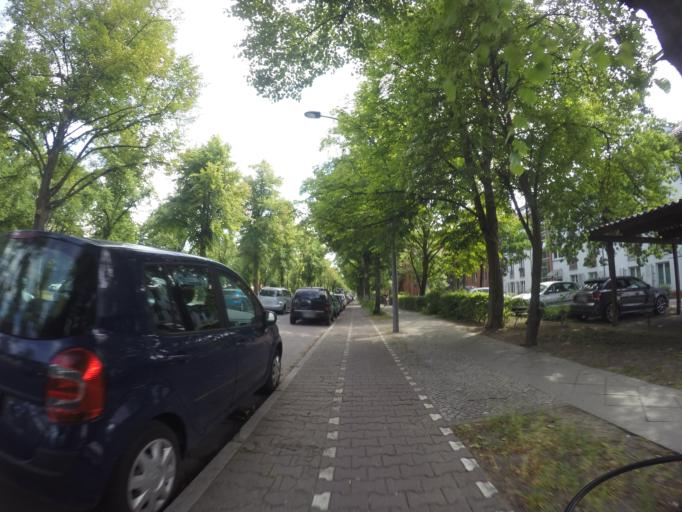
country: DE
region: Berlin
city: Lichtenrade
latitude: 52.3962
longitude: 13.4064
